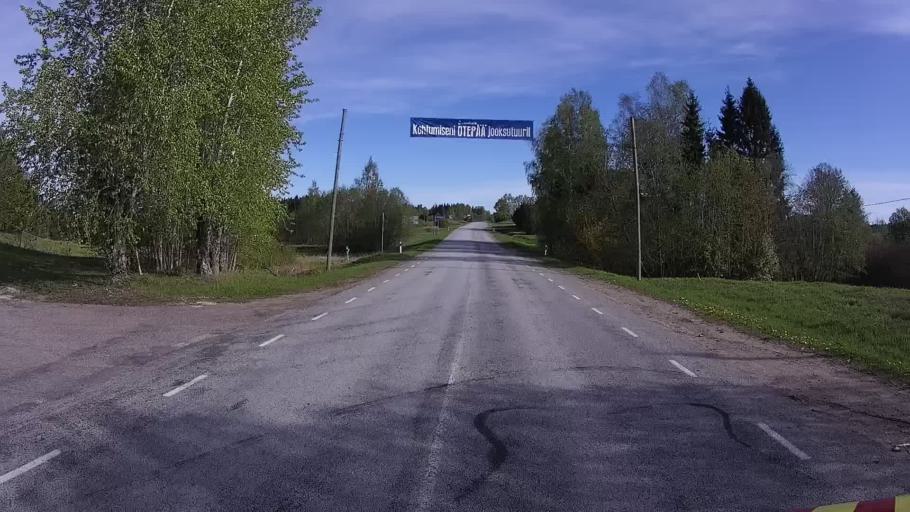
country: EE
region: Tartu
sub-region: Elva linn
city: Elva
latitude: 58.0673
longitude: 26.4998
